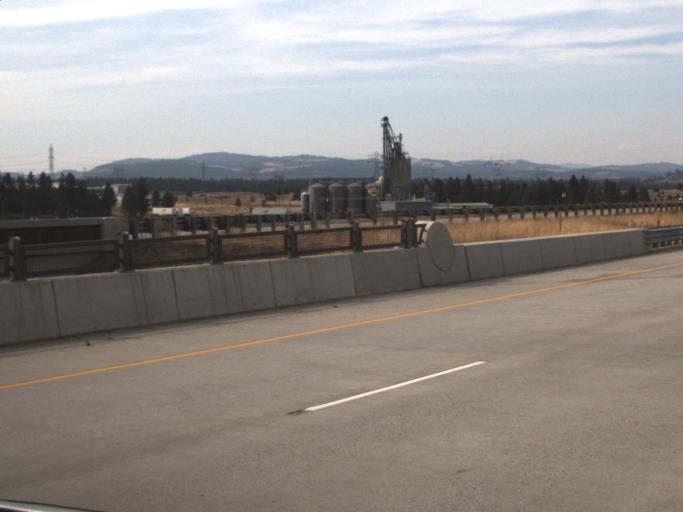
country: US
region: Washington
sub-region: Spokane County
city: Mead
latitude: 47.7527
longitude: -117.3597
